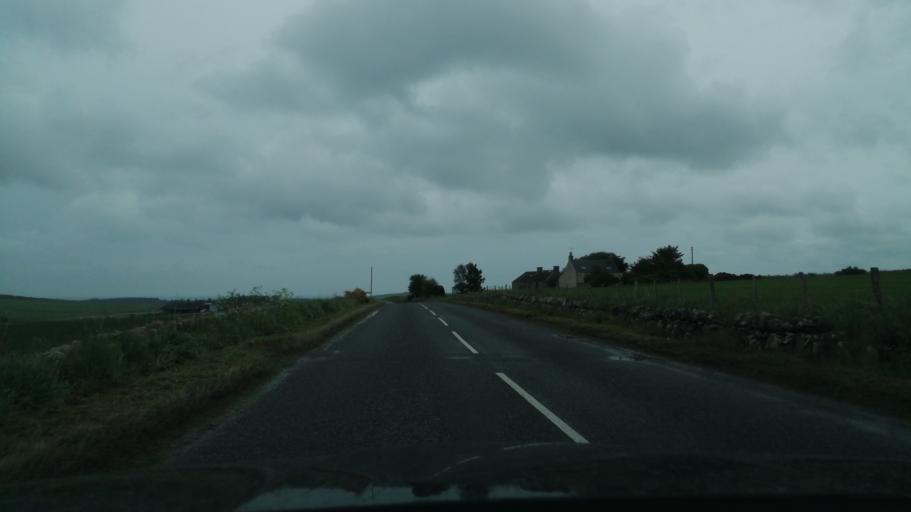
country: GB
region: Scotland
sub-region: Aberdeenshire
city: Portsoy
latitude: 57.6461
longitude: -2.7096
